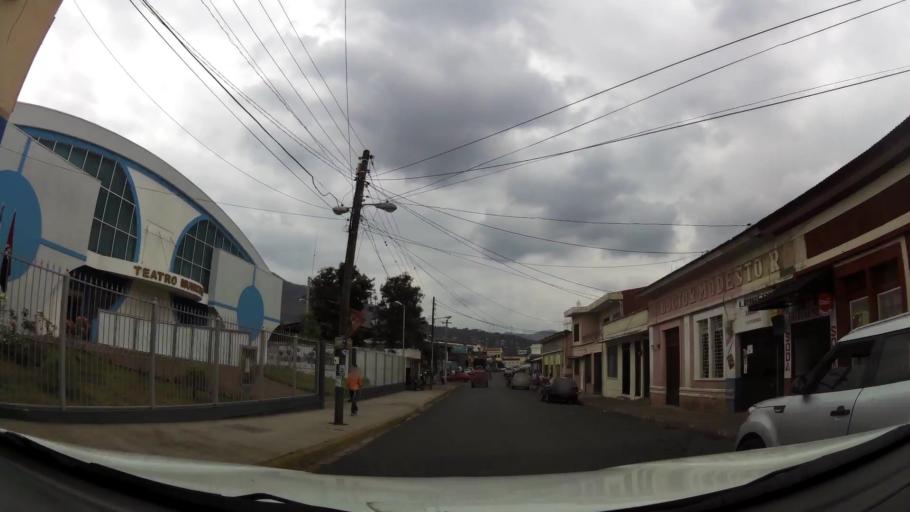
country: NI
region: Matagalpa
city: Matagalpa
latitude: 12.9299
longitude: -85.9178
